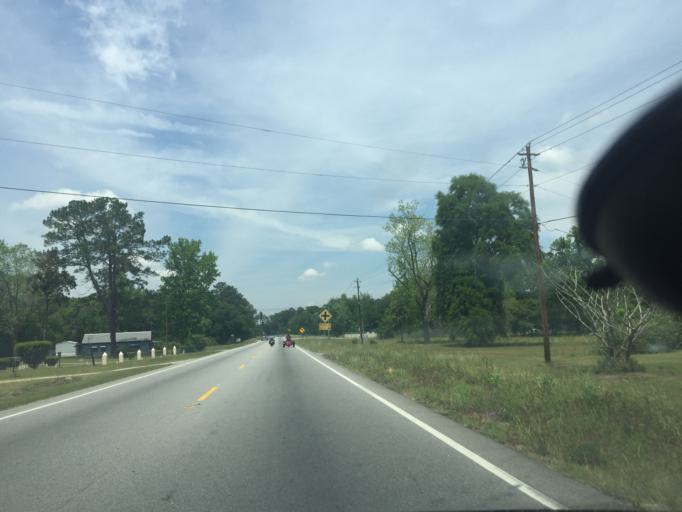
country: US
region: Georgia
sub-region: Chatham County
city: Bloomingdale
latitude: 32.1872
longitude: -81.4025
